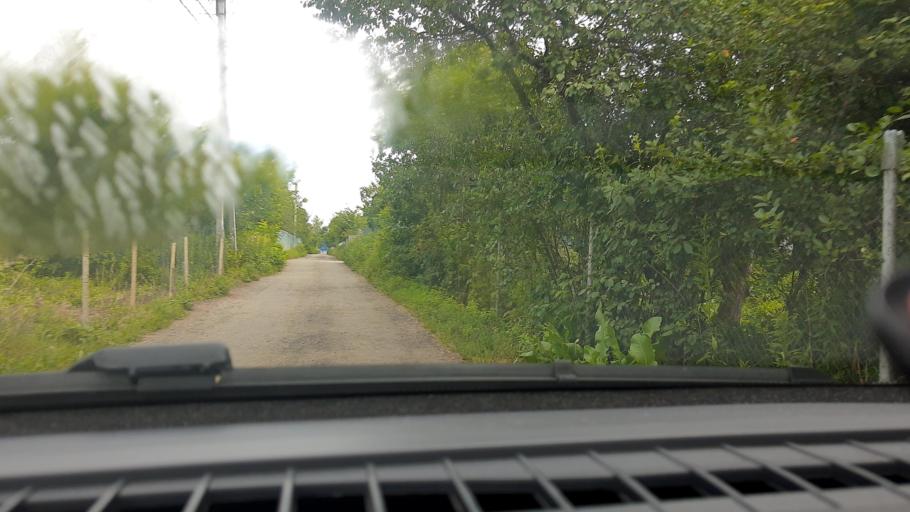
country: RU
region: Nizjnij Novgorod
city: Gorbatovka
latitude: 56.2425
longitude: 43.8176
